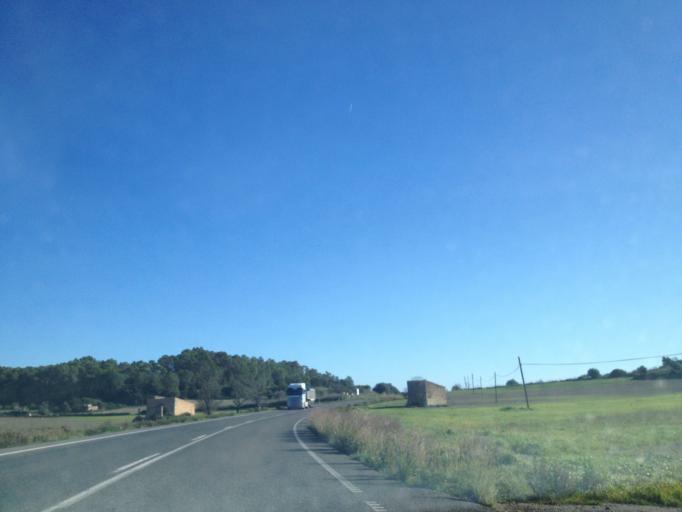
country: ES
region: Balearic Islands
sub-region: Illes Balears
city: Sineu
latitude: 39.6444
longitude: 3.0377
